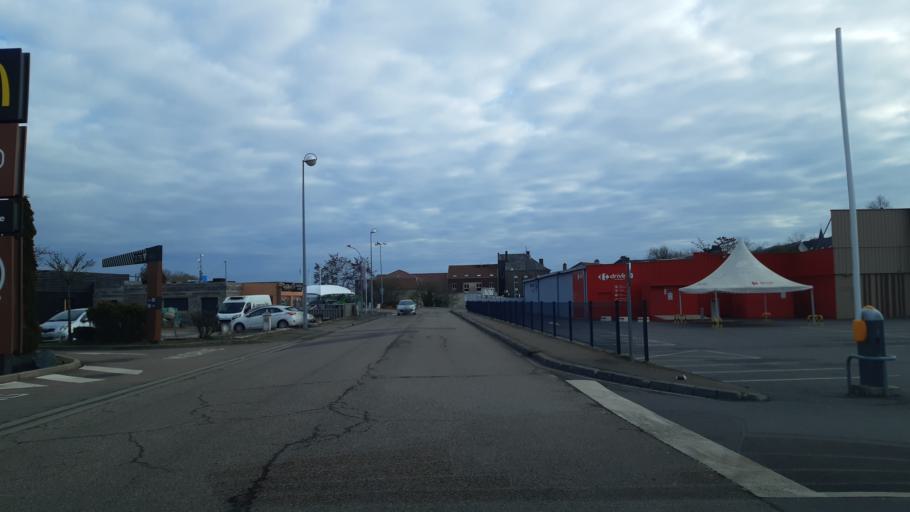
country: FR
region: Lorraine
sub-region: Departement de la Moselle
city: Audun-le-Tiche
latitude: 49.4760
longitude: 5.9557
